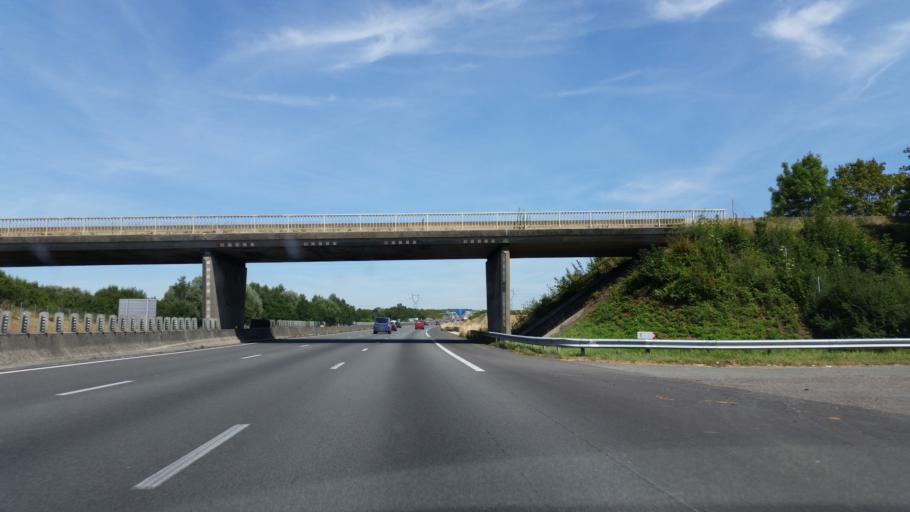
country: FR
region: Picardie
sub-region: Departement de la Somme
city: Peronne
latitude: 49.9609
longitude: 2.8559
